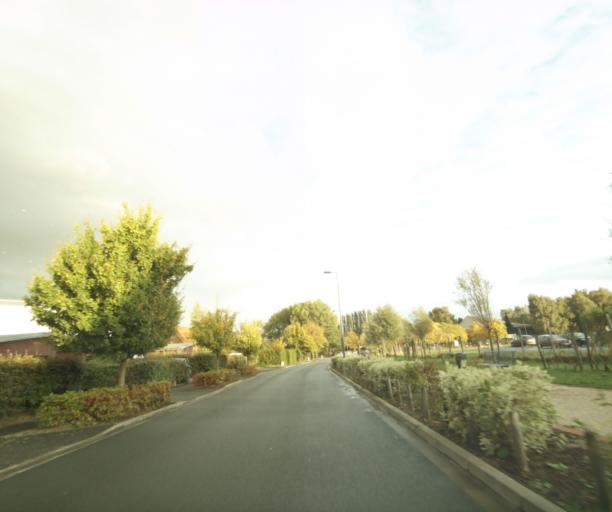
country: FR
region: Nord-Pas-de-Calais
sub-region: Departement du Nord
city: Wasquehal
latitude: 50.6535
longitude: 3.1418
